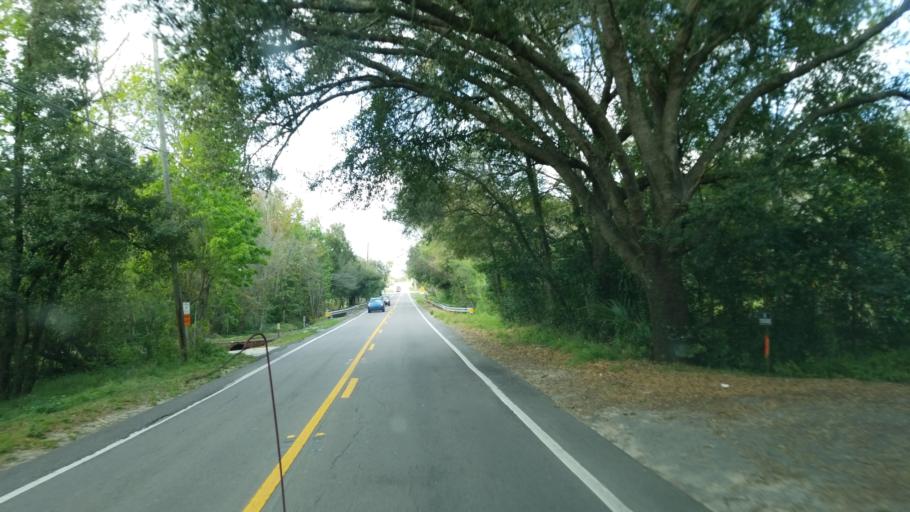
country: US
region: Florida
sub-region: Polk County
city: Haines City
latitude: 28.1112
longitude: -81.6068
